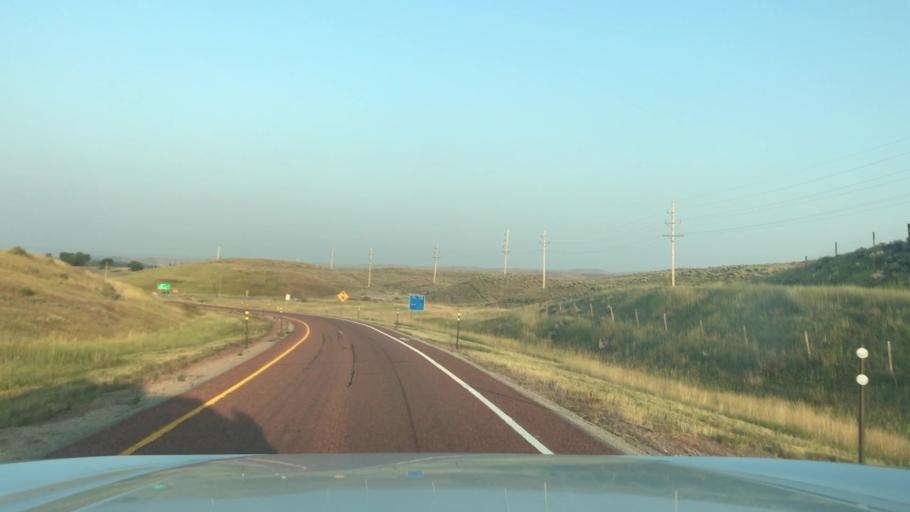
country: US
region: Wyoming
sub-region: Sheridan County
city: Sheridan
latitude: 44.9151
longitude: -107.1556
